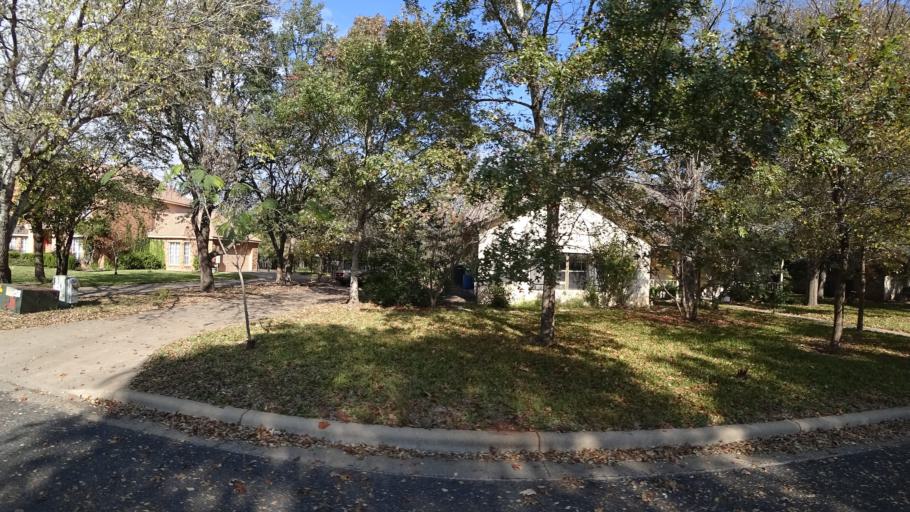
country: US
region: Texas
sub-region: Travis County
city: Shady Hollow
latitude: 30.1660
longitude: -97.8685
